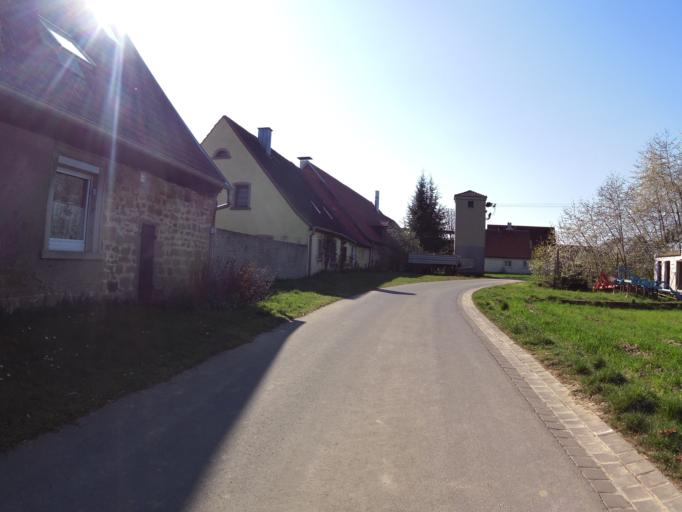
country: DE
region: Bavaria
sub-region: Regierungsbezirk Unterfranken
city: Prosselsheim
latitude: 49.8244
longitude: 10.1082
